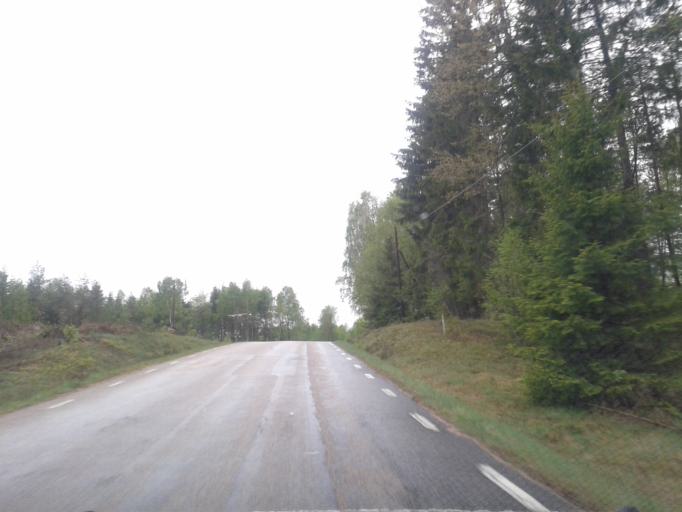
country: SE
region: Vaestra Goetaland
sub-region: Lilla Edets Kommun
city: Lodose
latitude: 58.0763
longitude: 12.0299
